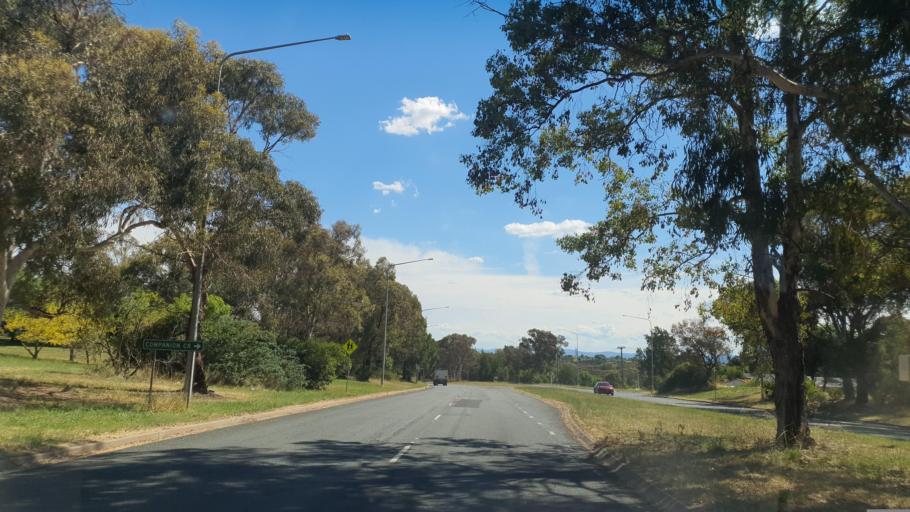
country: AU
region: Australian Capital Territory
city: Belconnen
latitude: -35.2129
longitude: 149.0472
